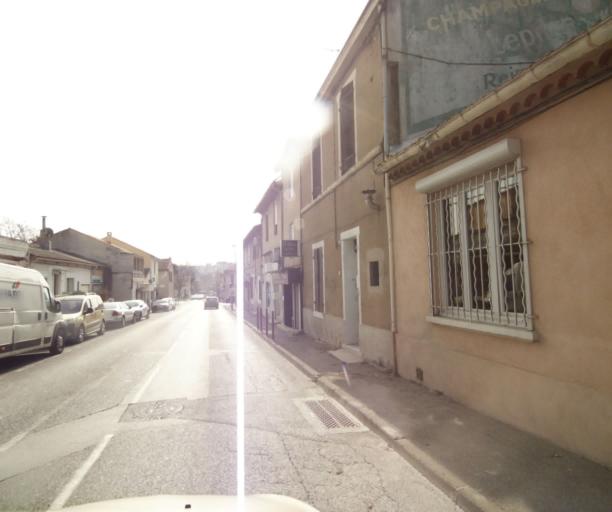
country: FR
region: Provence-Alpes-Cote d'Azur
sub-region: Departement des Bouches-du-Rhone
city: Marseille 15
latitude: 43.3861
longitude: 5.3459
